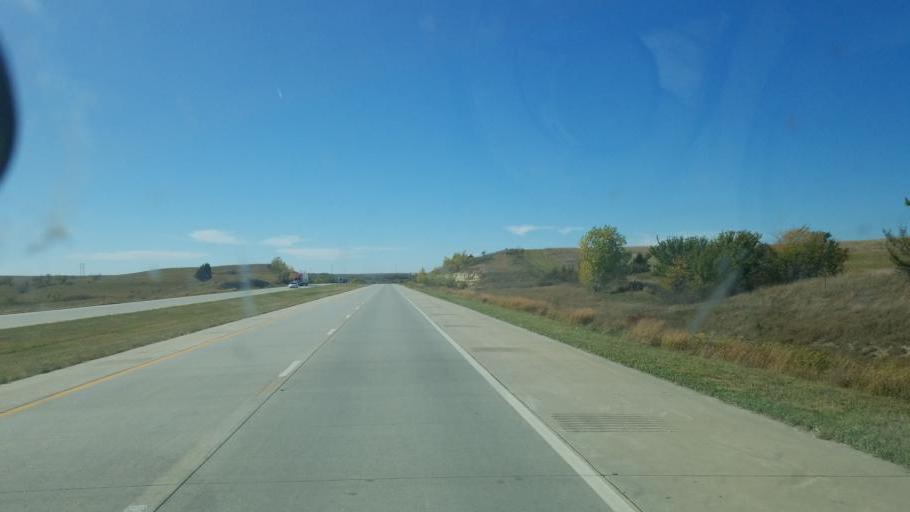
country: US
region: Kansas
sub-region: Riley County
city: Ogden
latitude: 39.0660
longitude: -96.6035
